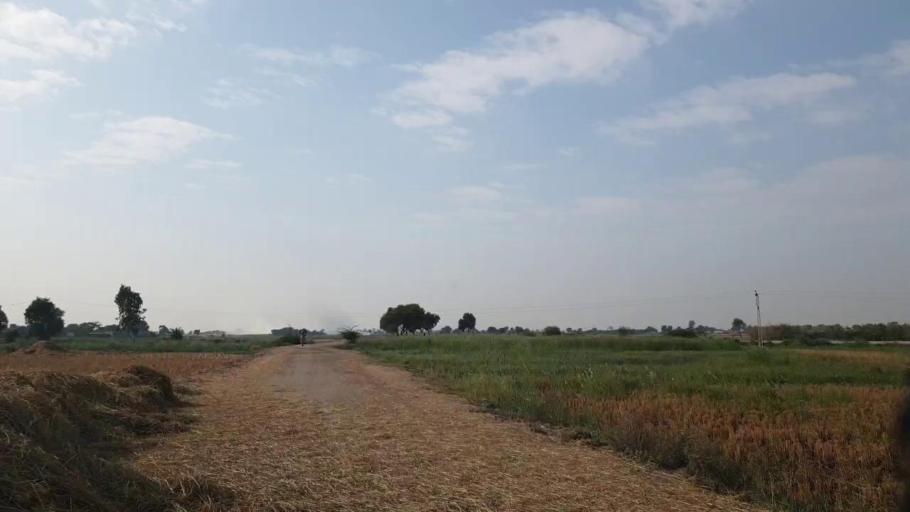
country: PK
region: Sindh
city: Tando Muhammad Khan
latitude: 25.0524
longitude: 68.4278
